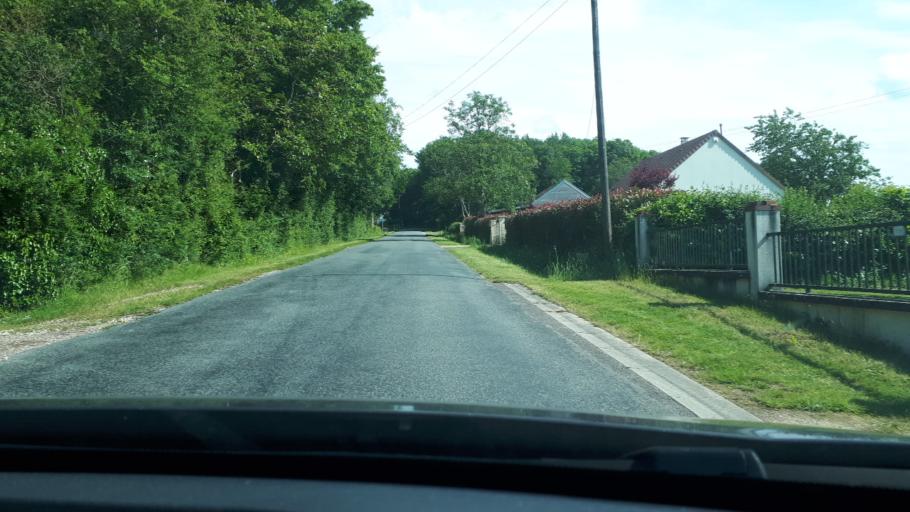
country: FR
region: Centre
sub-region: Departement du Cher
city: Blancafort
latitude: 47.4245
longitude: 2.6065
